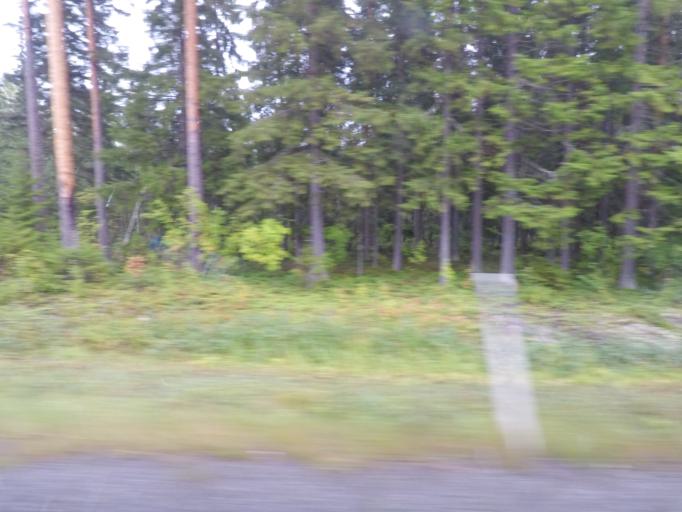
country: FI
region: Southern Savonia
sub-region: Pieksaemaeki
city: Juva
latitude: 62.0253
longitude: 27.7996
